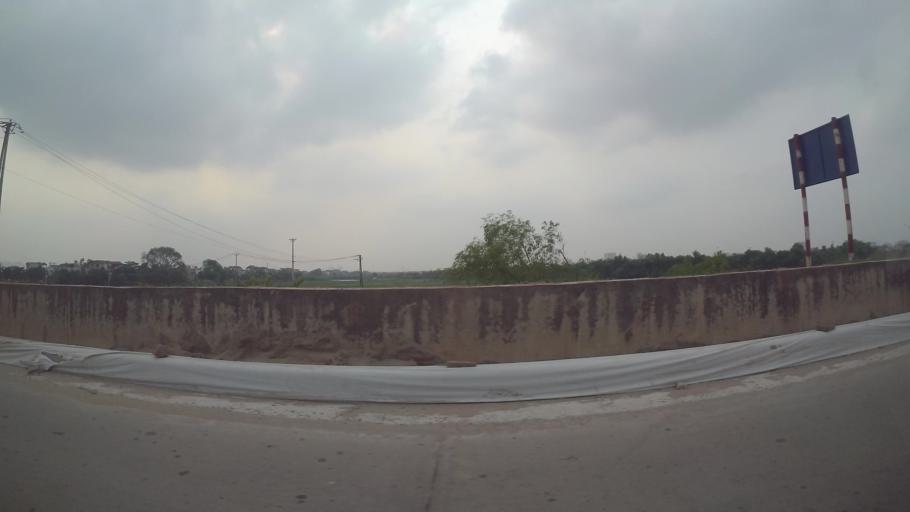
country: VN
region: Ha Noi
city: Trau Quy
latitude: 21.0126
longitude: 105.9044
